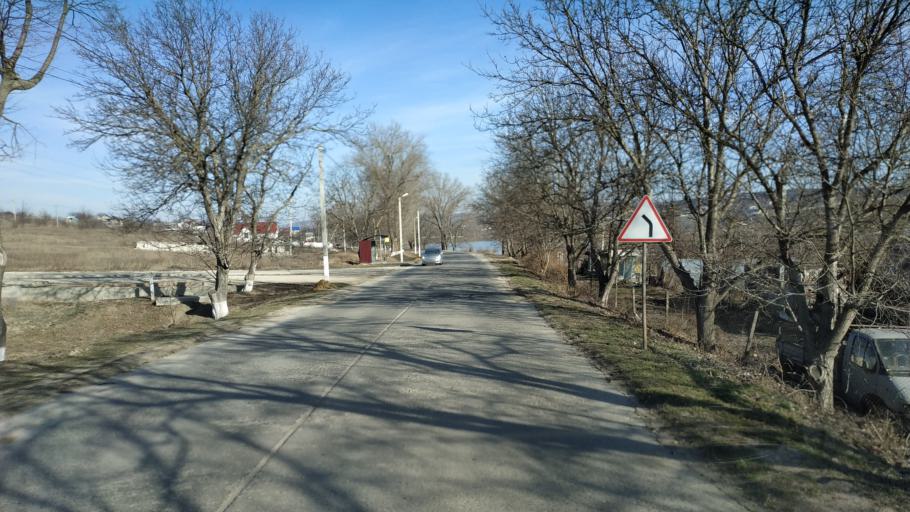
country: MD
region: Chisinau
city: Vatra
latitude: 46.9975
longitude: 28.6741
